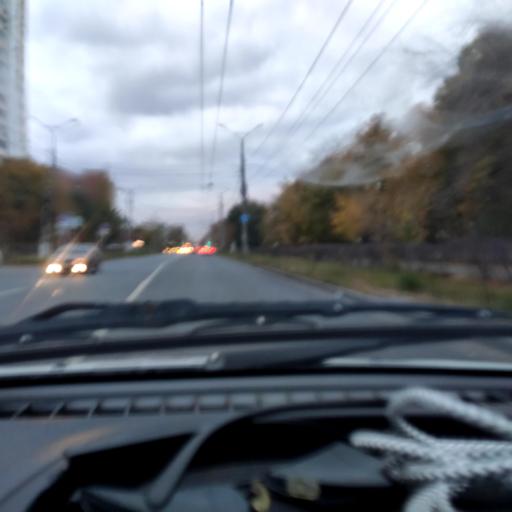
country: RU
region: Samara
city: Tol'yatti
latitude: 53.5196
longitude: 49.4157
